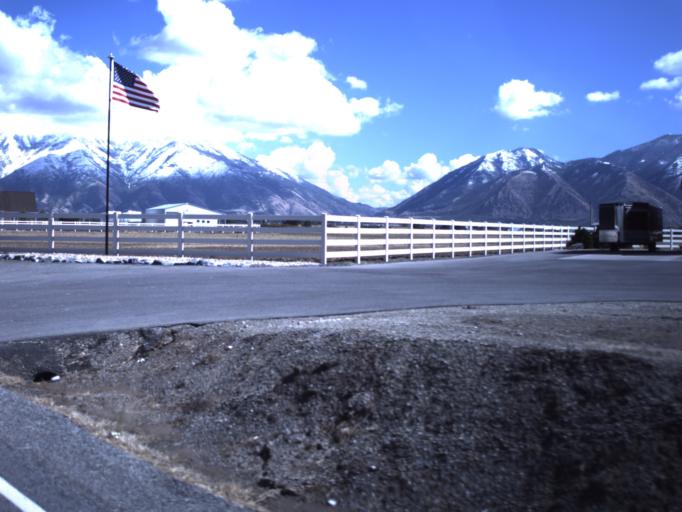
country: US
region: Utah
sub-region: Utah County
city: Benjamin
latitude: 40.1153
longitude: -111.6954
